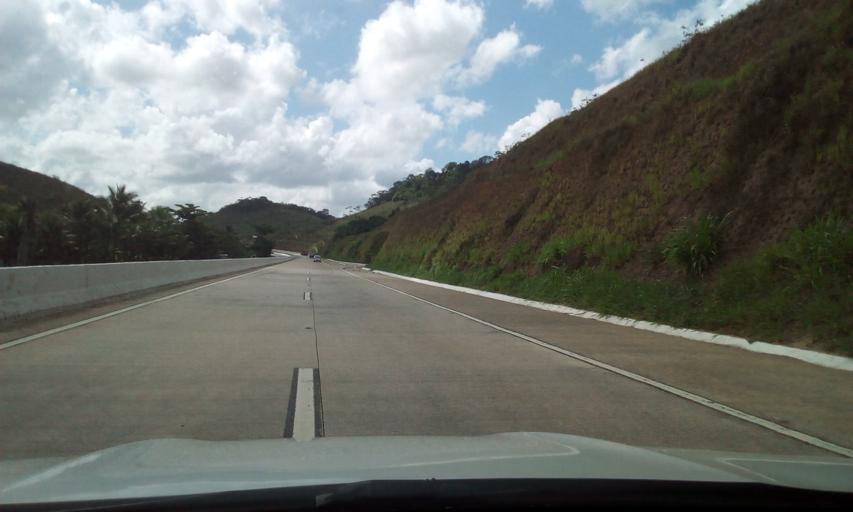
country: BR
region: Pernambuco
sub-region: Palmares
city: Palmares
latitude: -8.7378
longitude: -35.6095
